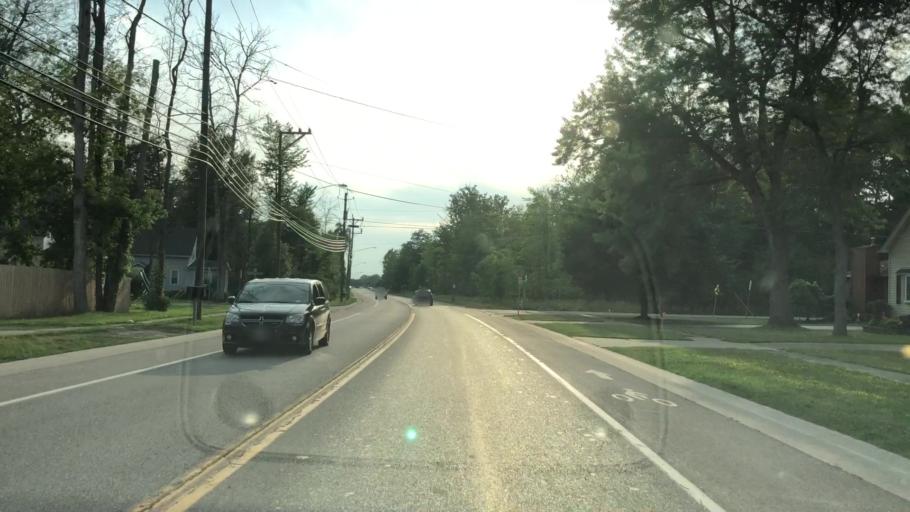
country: US
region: New York
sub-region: Erie County
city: Cheektowaga
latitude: 42.8930
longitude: -78.7449
